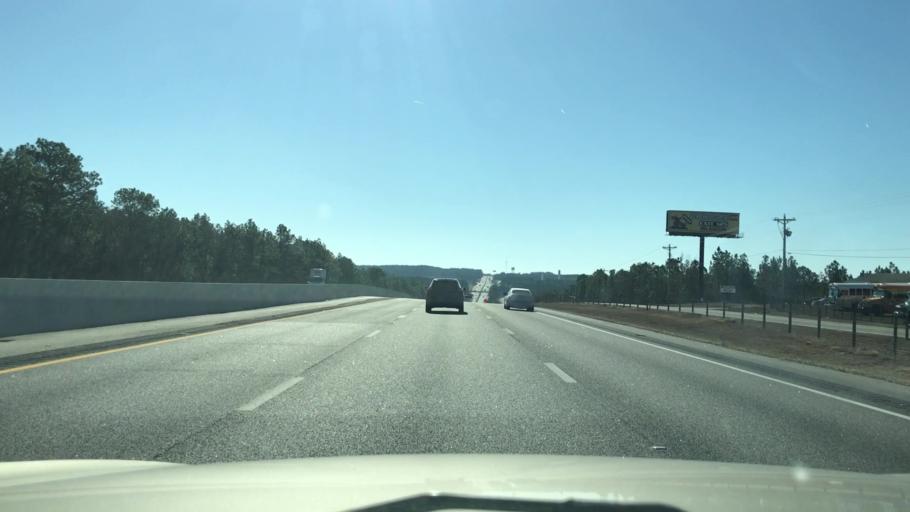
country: US
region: South Carolina
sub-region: Lexington County
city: Gaston
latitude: 33.8625
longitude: -81.0313
